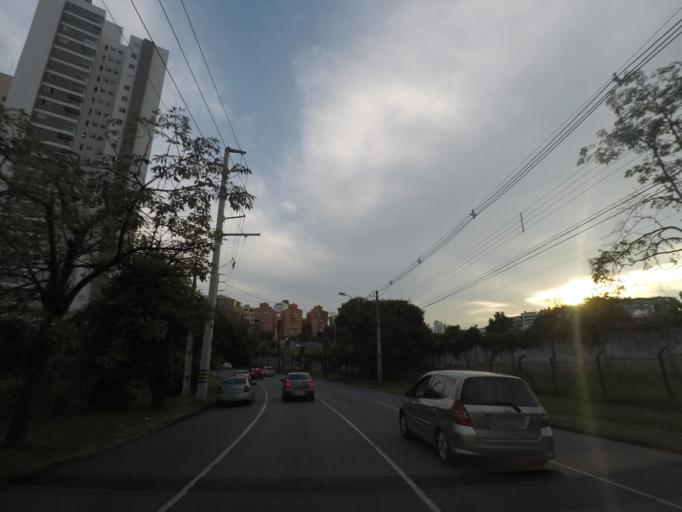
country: BR
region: Parana
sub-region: Curitiba
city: Curitiba
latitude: -25.4051
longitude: -49.2537
